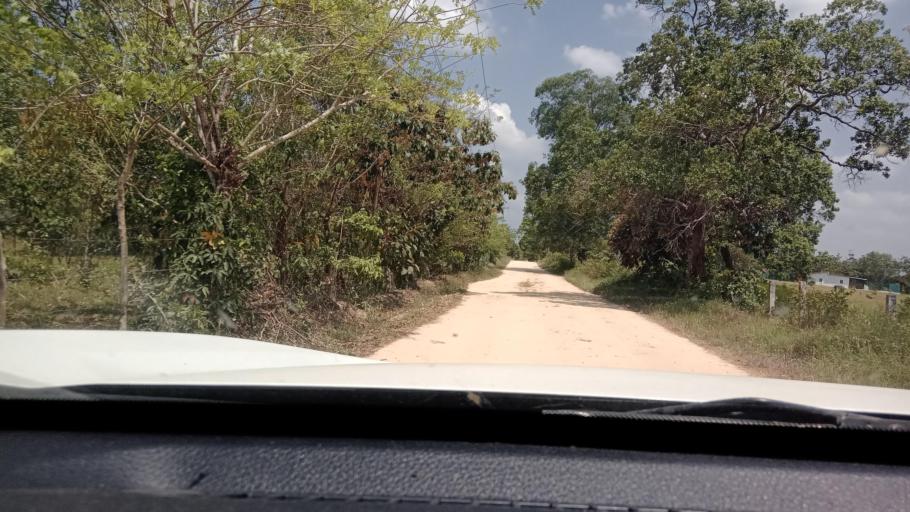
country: MX
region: Veracruz
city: Las Choapas
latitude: 17.9414
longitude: -94.1222
